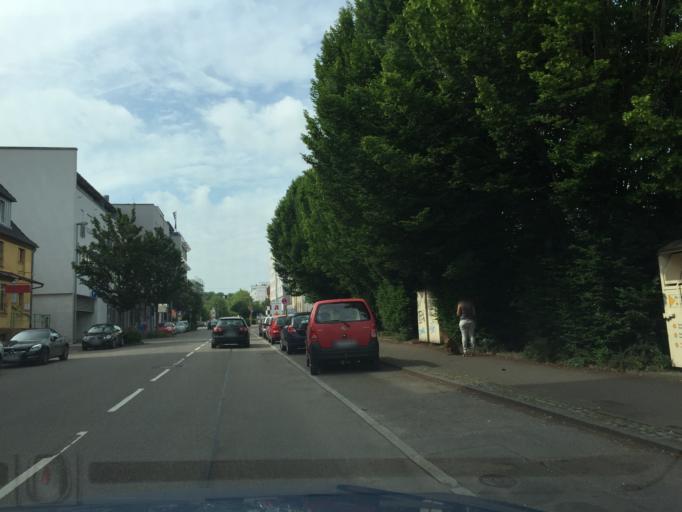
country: DE
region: Baden-Wuerttemberg
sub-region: Tuebingen Region
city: Ulm
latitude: 48.3957
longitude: 9.9643
